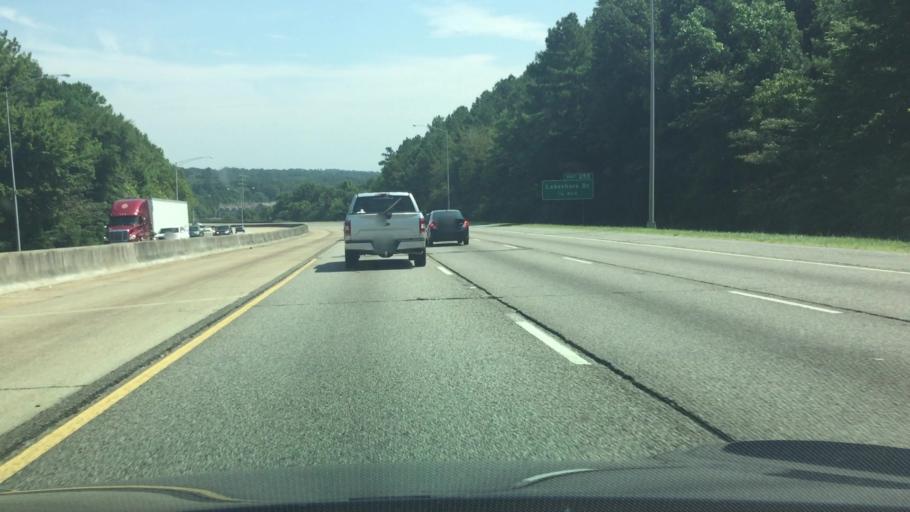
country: US
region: Alabama
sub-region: Jefferson County
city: Vestavia Hills
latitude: 33.4433
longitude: -86.8200
